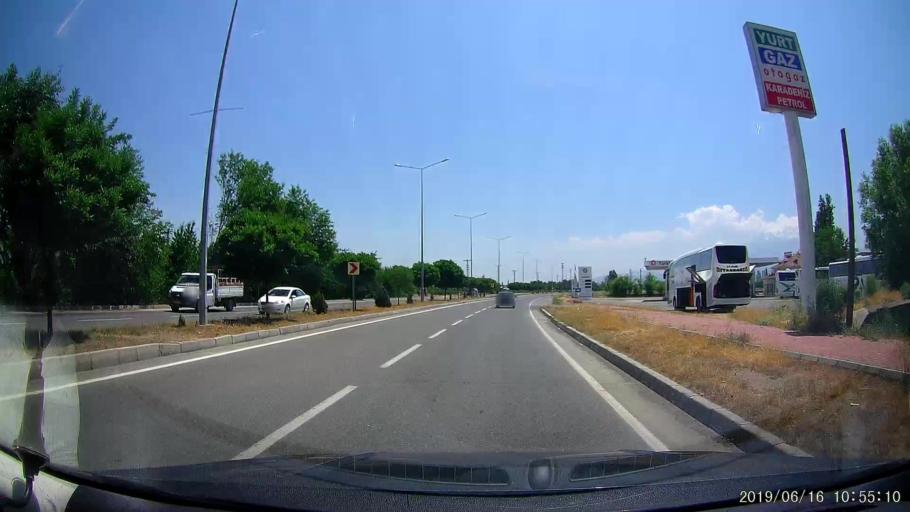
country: TR
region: Igdir
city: Igdir
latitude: 39.9374
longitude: 44.0072
